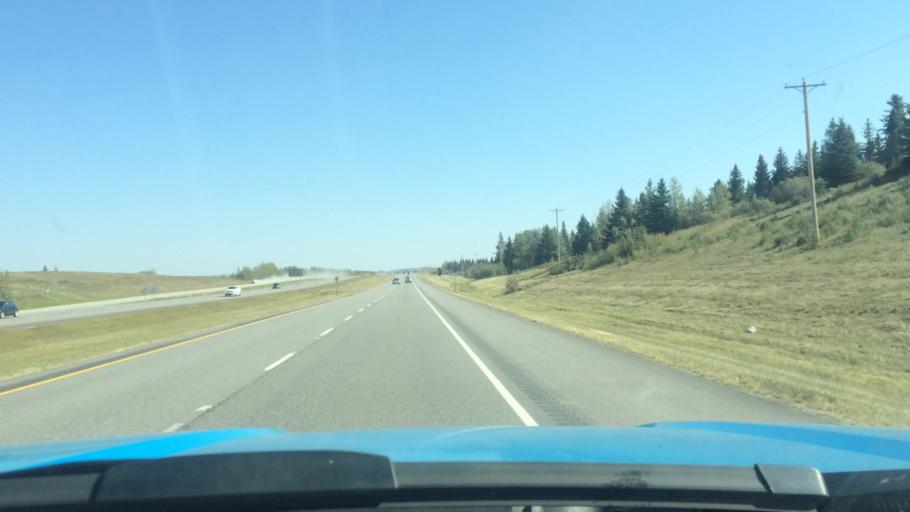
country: CA
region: Alberta
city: Cochrane
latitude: 51.1280
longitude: -114.6869
